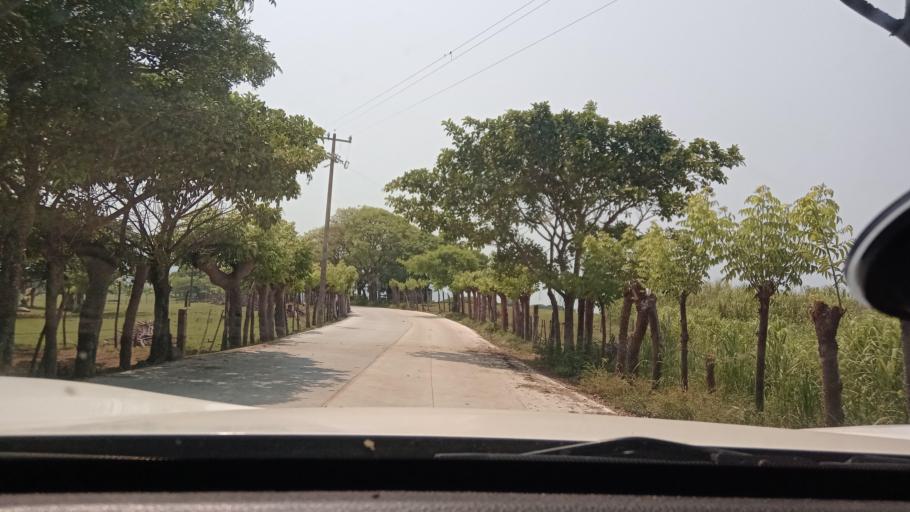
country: MX
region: Veracruz
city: Catemaco
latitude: 18.5578
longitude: -95.0186
